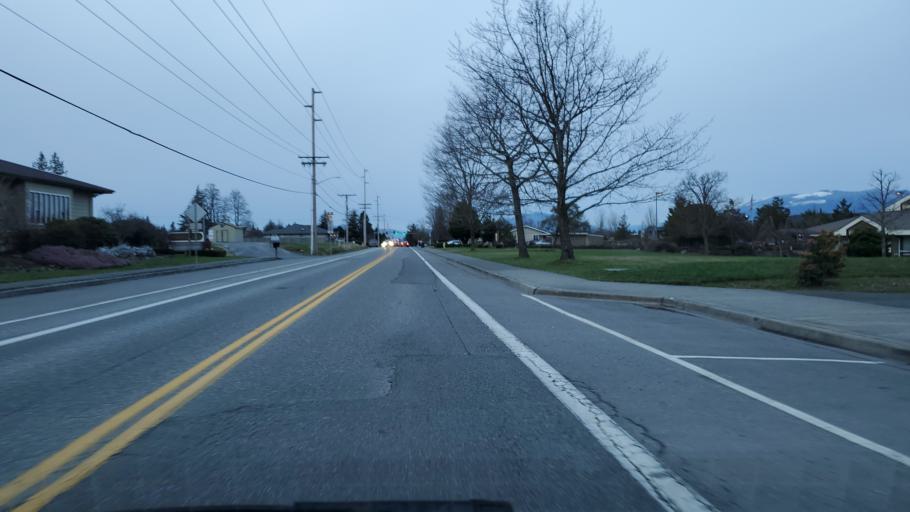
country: US
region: Washington
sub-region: Skagit County
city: Mount Vernon
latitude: 48.4185
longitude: -122.3188
